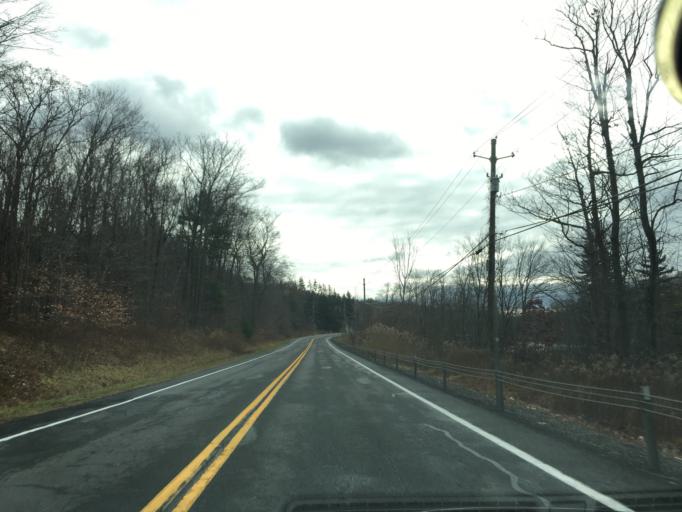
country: US
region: New York
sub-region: Rensselaer County
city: Averill Park
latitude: 42.6193
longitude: -73.5252
